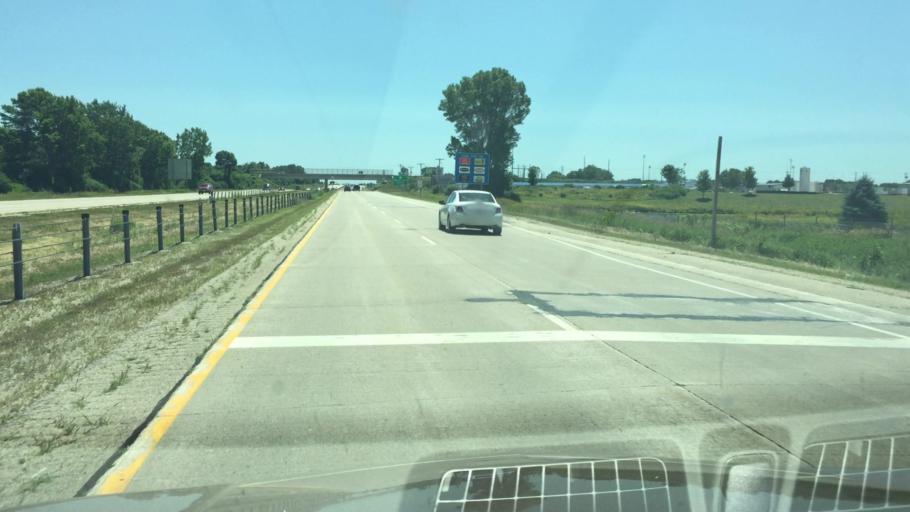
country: US
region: Wisconsin
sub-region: Dodge County
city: Beaver Dam
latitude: 43.4703
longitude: -88.8154
